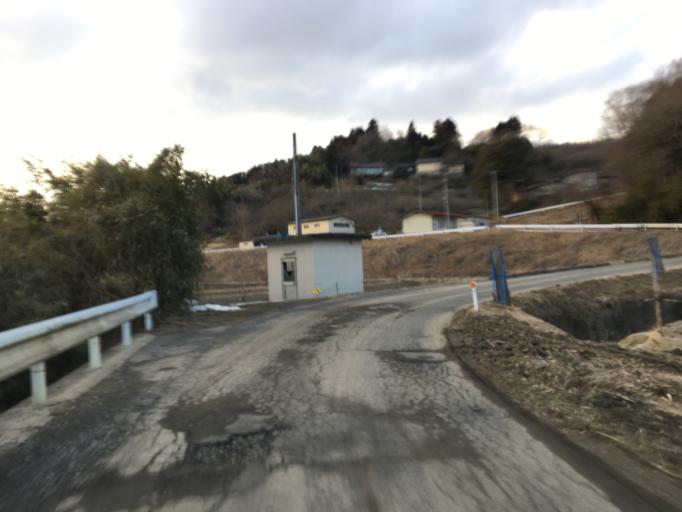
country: JP
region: Fukushima
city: Fukushima-shi
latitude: 37.6548
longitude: 140.5506
